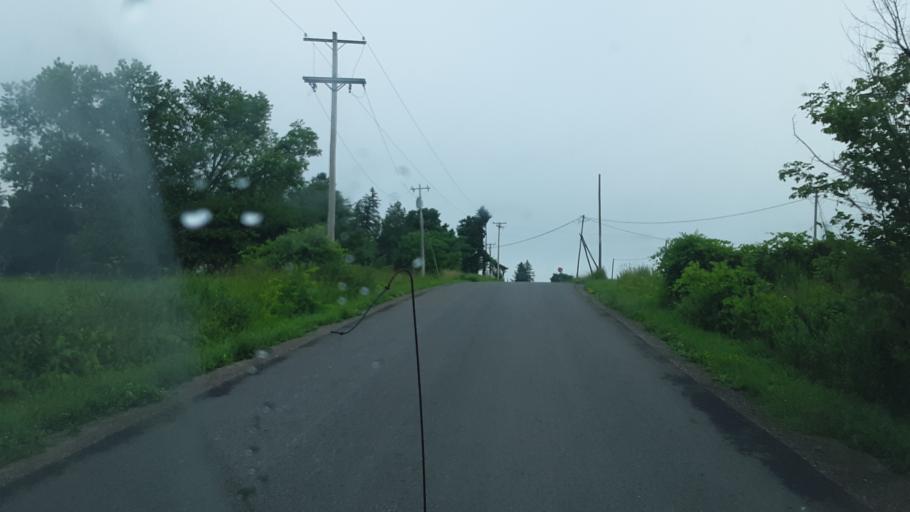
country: US
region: New York
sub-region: Montgomery County
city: Fonda
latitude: 42.8937
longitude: -74.3826
